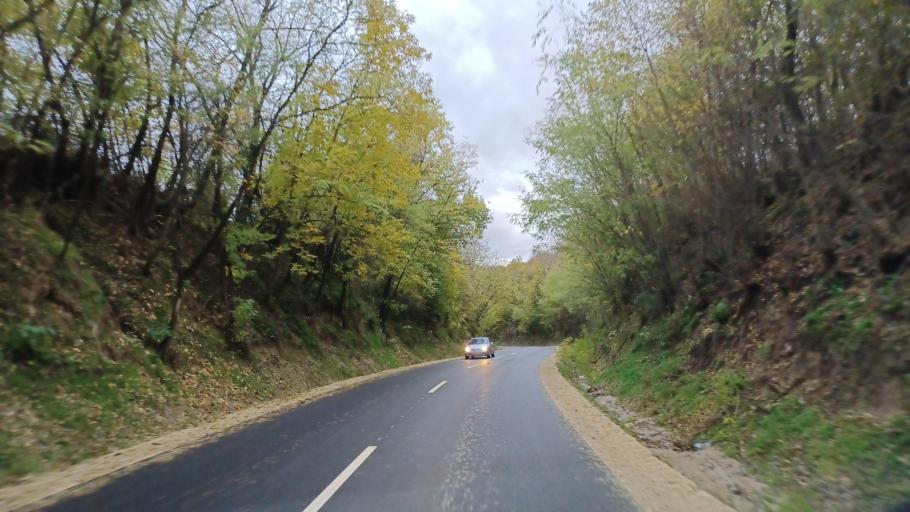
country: HU
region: Tolna
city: Gyonk
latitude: 46.5731
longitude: 18.4591
